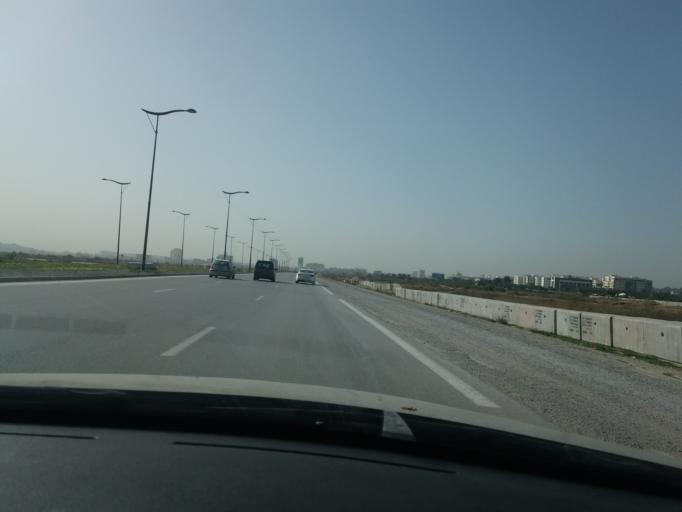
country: TN
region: Ariana
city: Ariana
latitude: 36.8241
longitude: 10.2046
